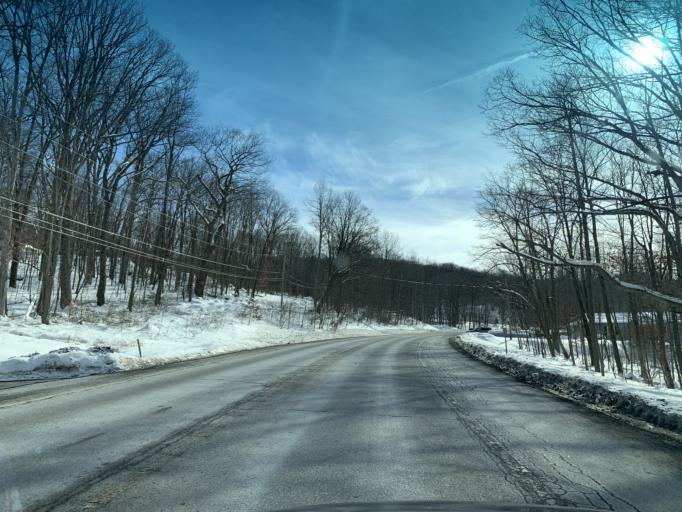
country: US
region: Maryland
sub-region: Allegany County
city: Frostburg
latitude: 39.6224
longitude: -78.8999
